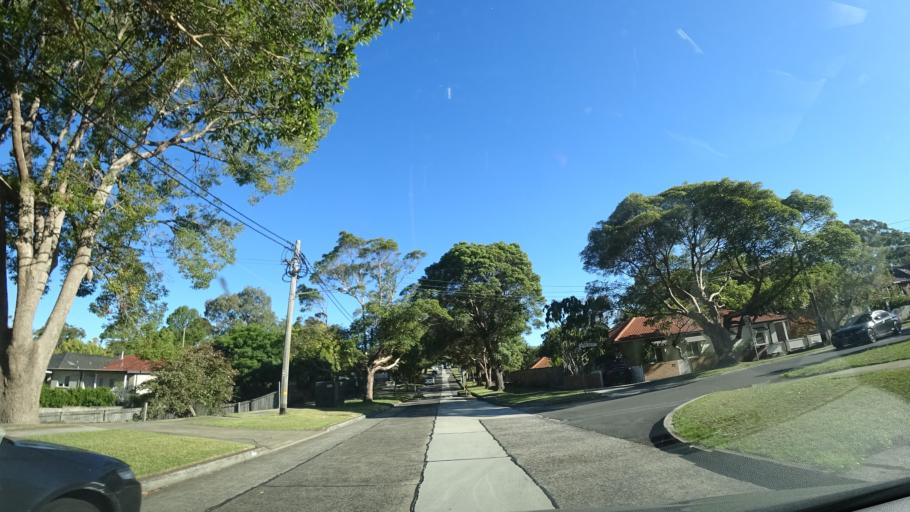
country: AU
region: New South Wales
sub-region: Willoughby
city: Chatswood
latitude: -33.7903
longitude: 151.1907
